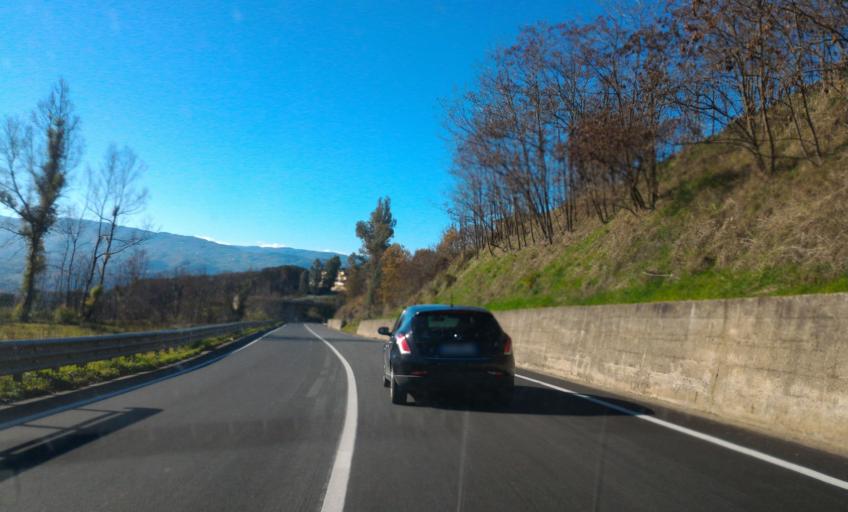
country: IT
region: Calabria
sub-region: Provincia di Cosenza
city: Rovito
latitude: 39.2985
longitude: 16.3094
